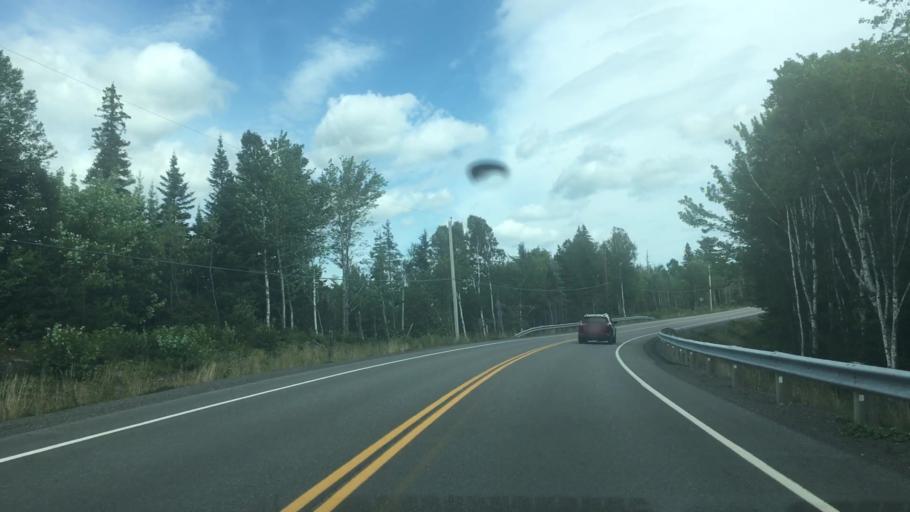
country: CA
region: Nova Scotia
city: Sydney Mines
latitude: 46.3098
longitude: -60.6165
